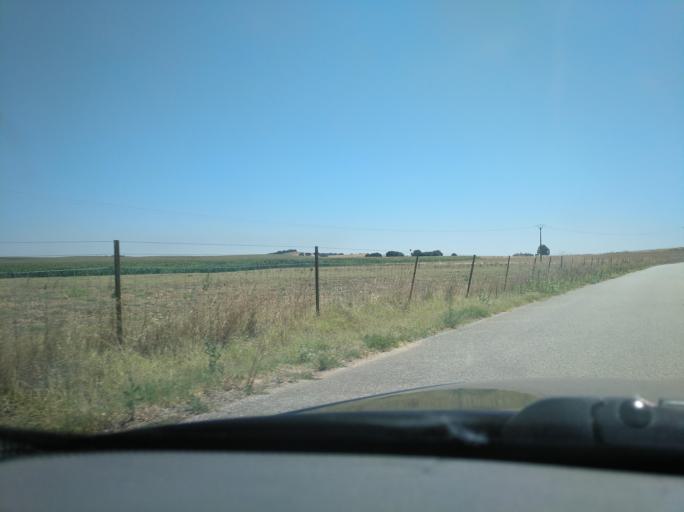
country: ES
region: Extremadura
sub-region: Provincia de Badajoz
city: Olivenza
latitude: 38.7289
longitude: -7.2182
